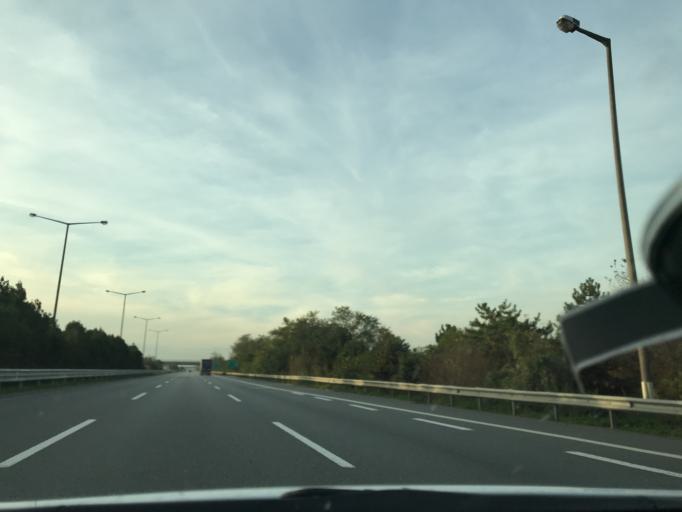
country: TR
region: Duzce
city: Cilimli
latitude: 40.8347
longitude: 31.0360
